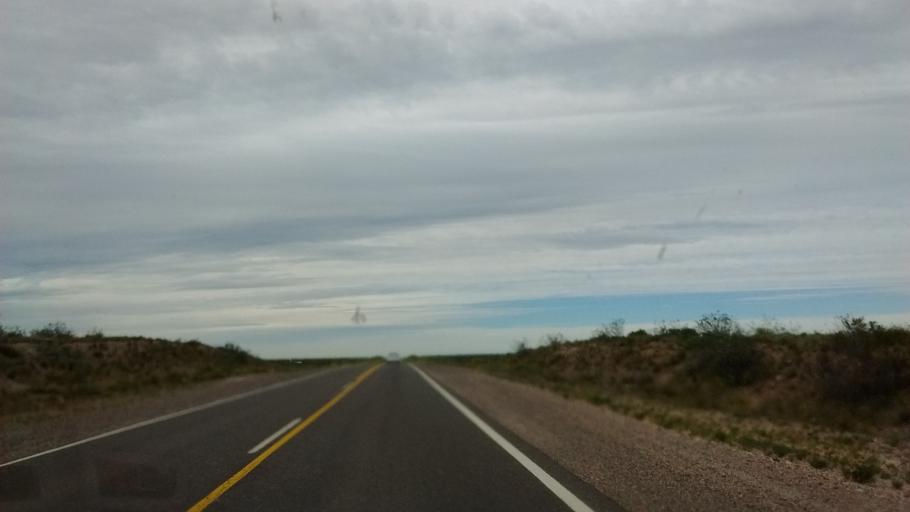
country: AR
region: Rio Negro
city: Catriel
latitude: -38.2827
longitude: -67.9959
